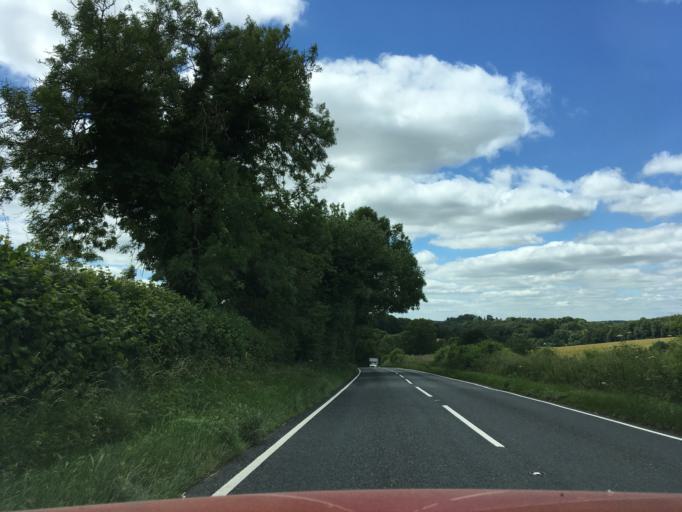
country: GB
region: England
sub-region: Hampshire
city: Highclere
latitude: 51.2993
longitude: -1.4065
